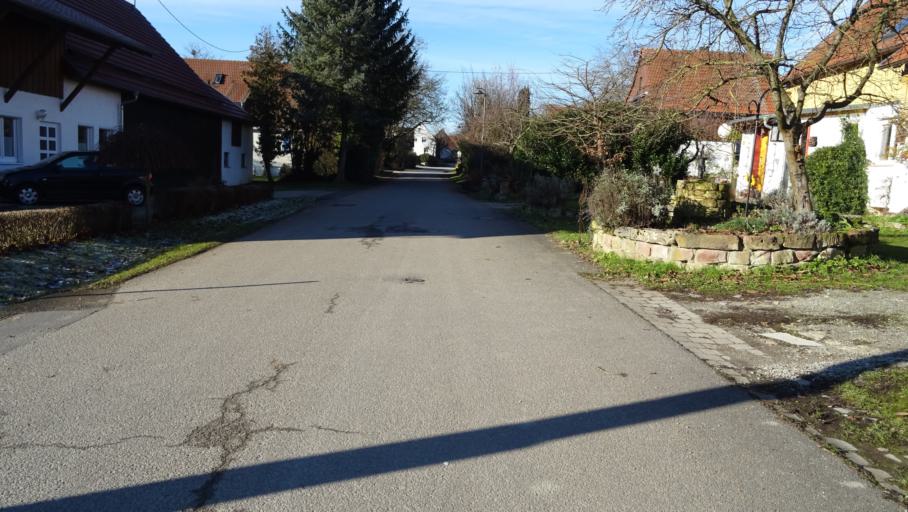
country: DE
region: Baden-Wuerttemberg
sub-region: Karlsruhe Region
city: Mosbach
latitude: 49.3448
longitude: 9.1794
